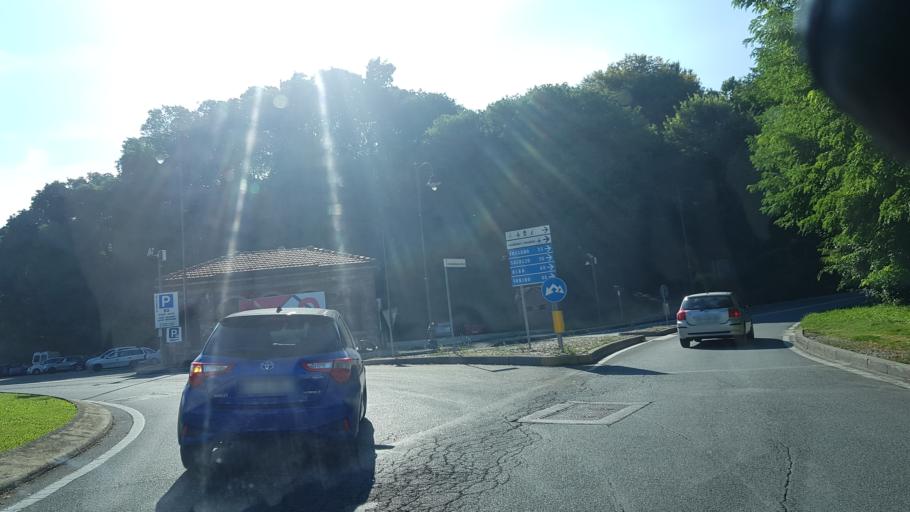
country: IT
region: Piedmont
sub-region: Provincia di Cuneo
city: Cuneo
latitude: 44.3926
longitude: 7.5552
